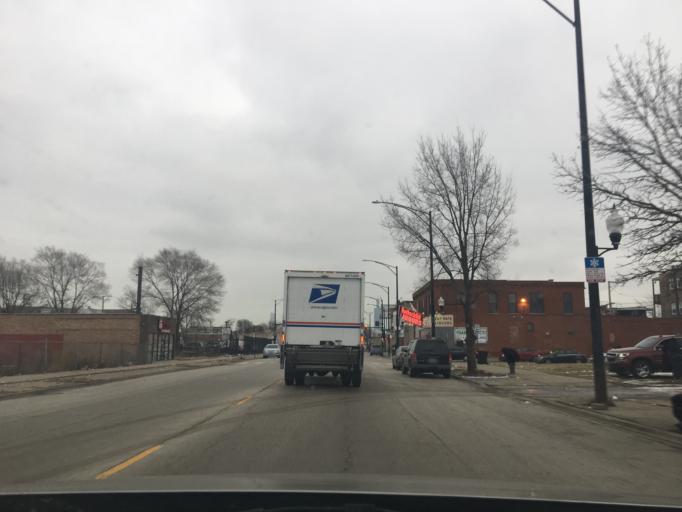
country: US
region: Illinois
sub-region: Cook County
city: Chicago
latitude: 41.8810
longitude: -87.7028
